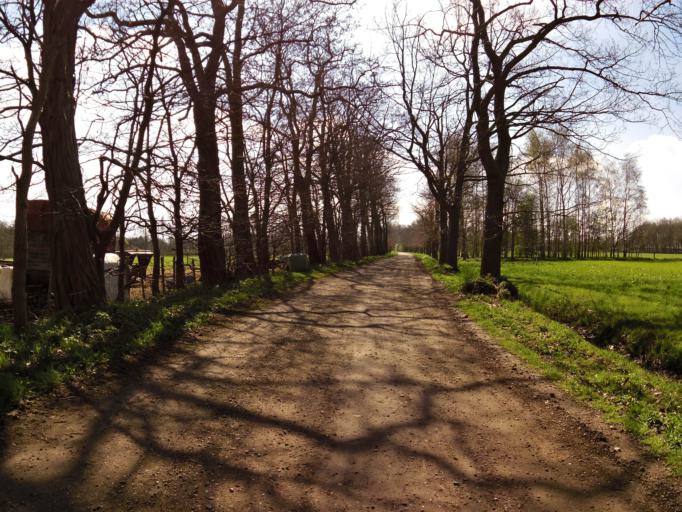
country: NL
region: North Brabant
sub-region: Gemeente Vught
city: Vught
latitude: 51.6188
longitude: 5.2782
